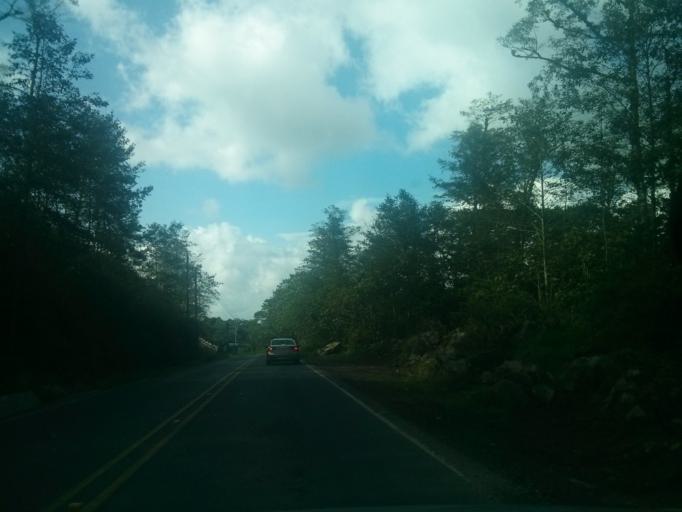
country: CR
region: Heredia
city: Santo Domingo
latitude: 10.1823
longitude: -84.1550
